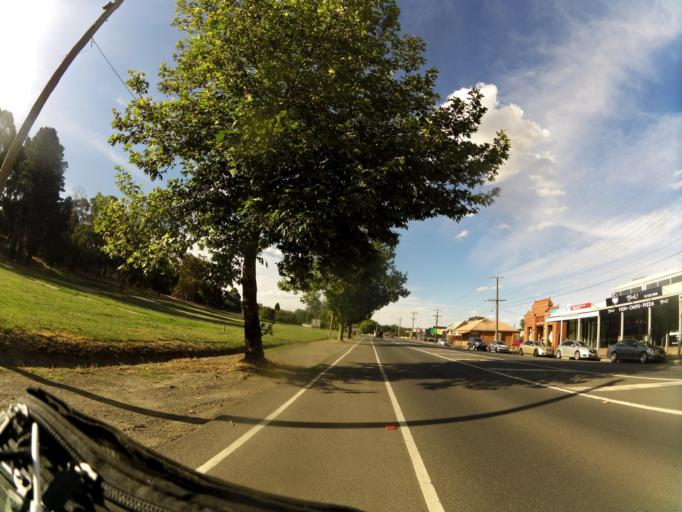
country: AU
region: Victoria
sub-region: Ballarat North
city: Golden Point
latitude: -37.5765
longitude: 143.8684
